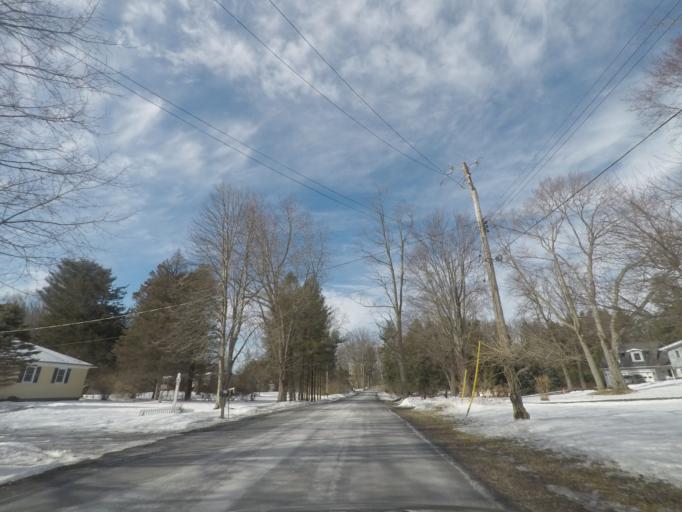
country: US
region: New York
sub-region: Albany County
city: Voorheesville
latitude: 42.6568
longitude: -73.9544
